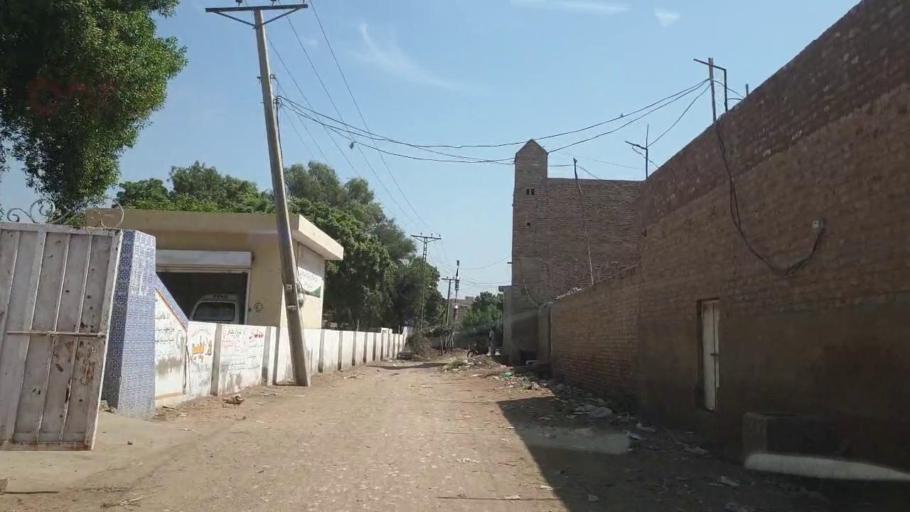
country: PK
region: Sindh
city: Tando Allahyar
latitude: 25.3897
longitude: 68.6746
